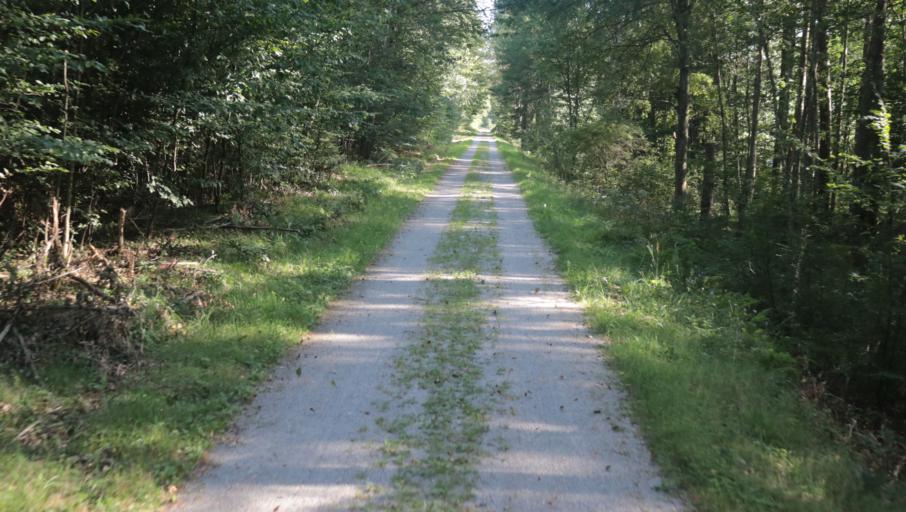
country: SE
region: Blekinge
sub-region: Karlshamns Kommun
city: Svangsta
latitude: 56.3660
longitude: 14.6863
